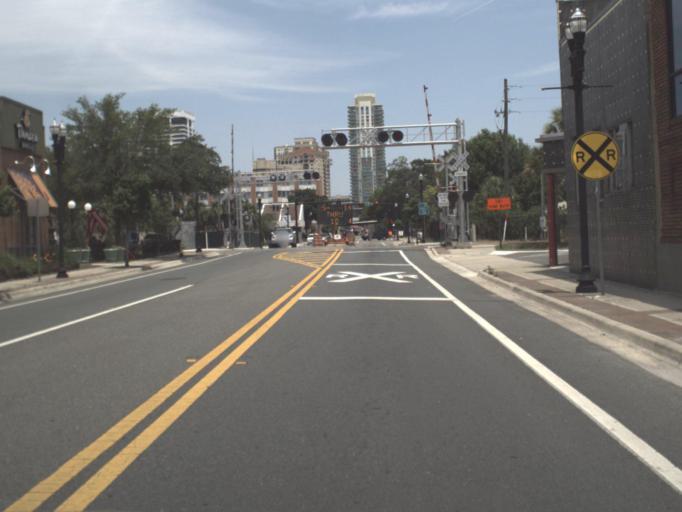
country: US
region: Florida
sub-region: Duval County
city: Jacksonville
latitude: 30.3106
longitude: -81.6547
